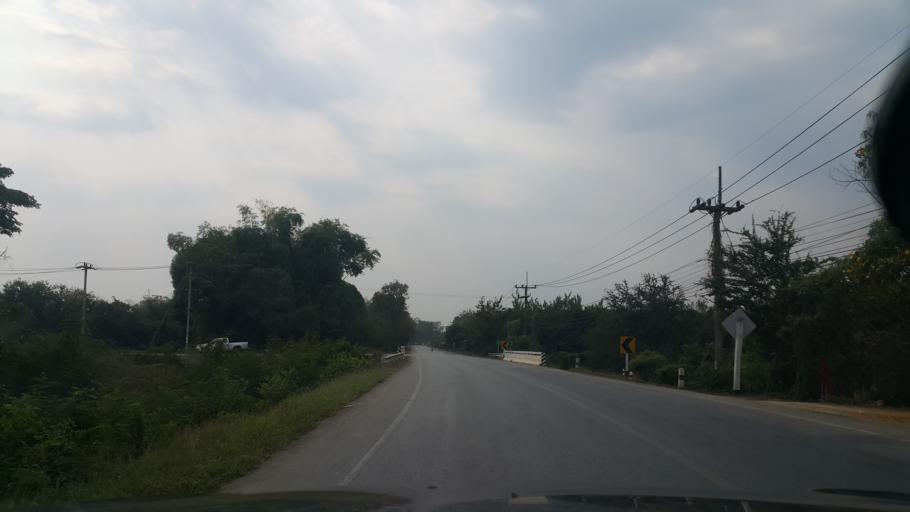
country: TH
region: Sukhothai
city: Si Samrong
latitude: 17.0810
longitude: 99.8808
